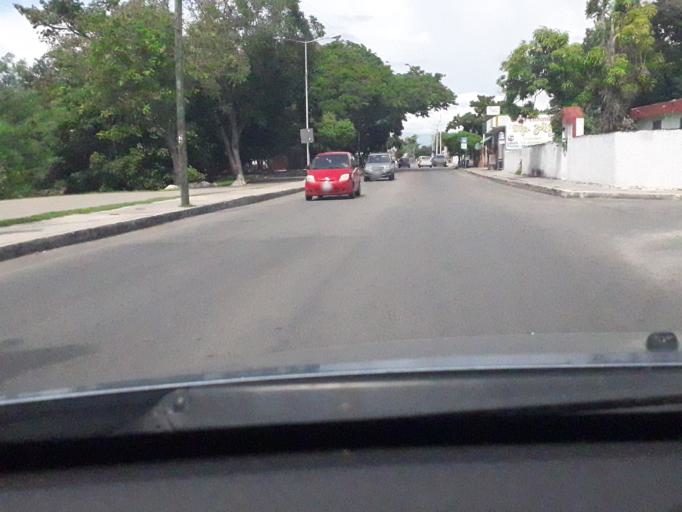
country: MX
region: Yucatan
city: Merida
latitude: 20.9750
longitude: -89.6556
